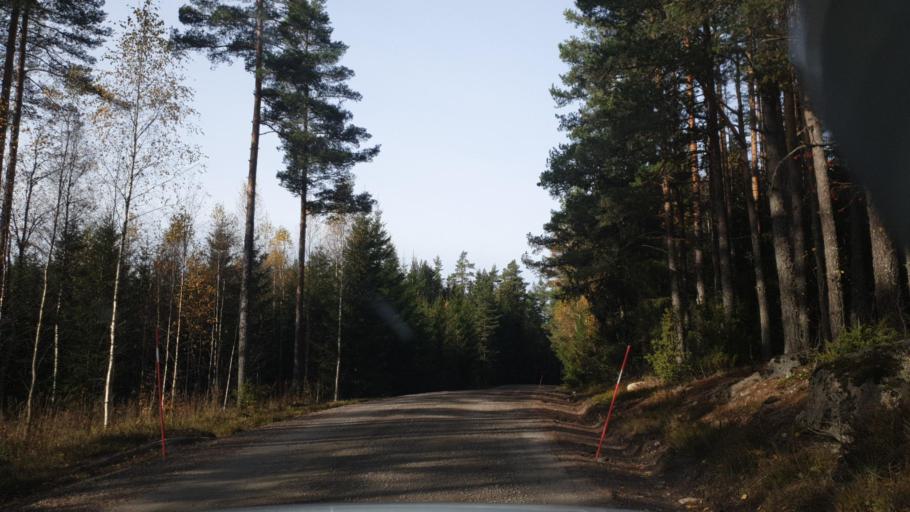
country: SE
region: Vaermland
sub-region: Eda Kommun
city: Charlottenberg
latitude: 59.7290
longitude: 12.1184
